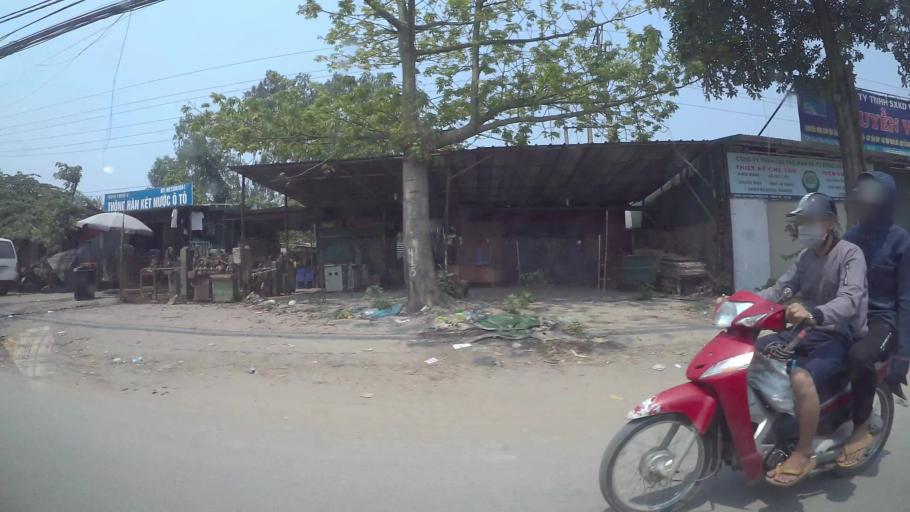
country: VN
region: Ha Noi
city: Van Dien
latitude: 20.9511
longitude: 105.8193
